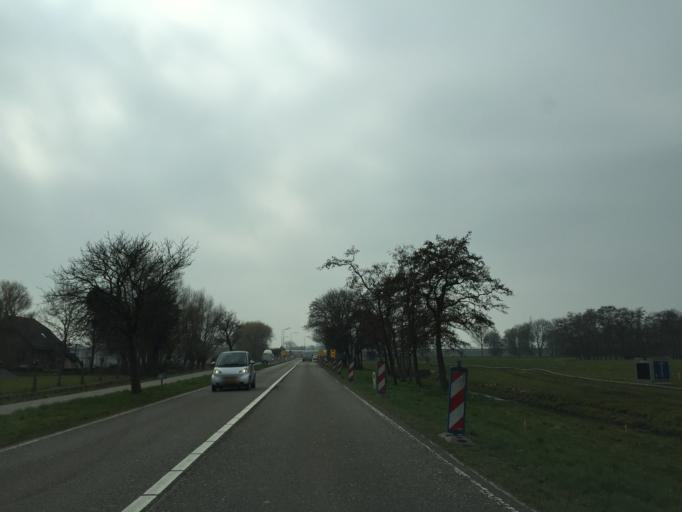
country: NL
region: South Holland
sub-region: Gemeente Westland
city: De Lier
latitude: 51.9874
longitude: 4.2862
